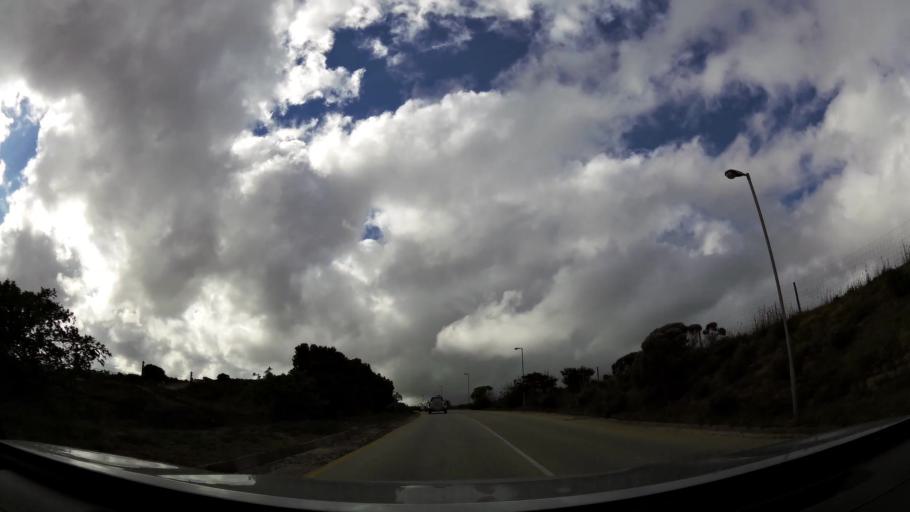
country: ZA
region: Western Cape
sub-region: Eden District Municipality
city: Knysna
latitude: -34.0730
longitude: 23.0860
